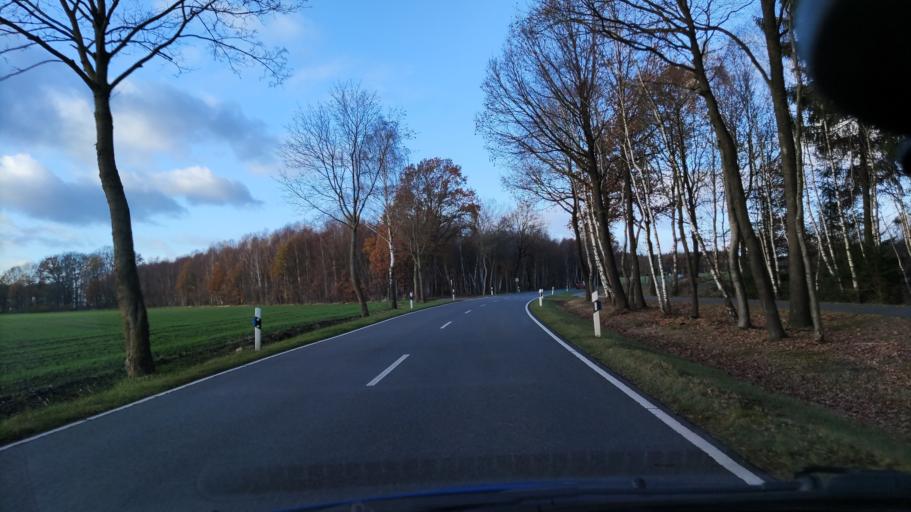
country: DE
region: Lower Saxony
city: Schneverdingen
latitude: 53.0537
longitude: 9.8212
